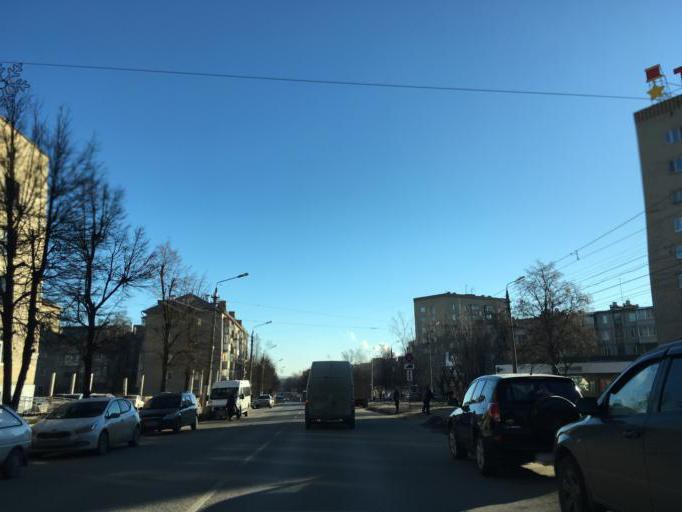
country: RU
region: Tula
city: Tula
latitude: 54.1890
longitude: 37.6914
